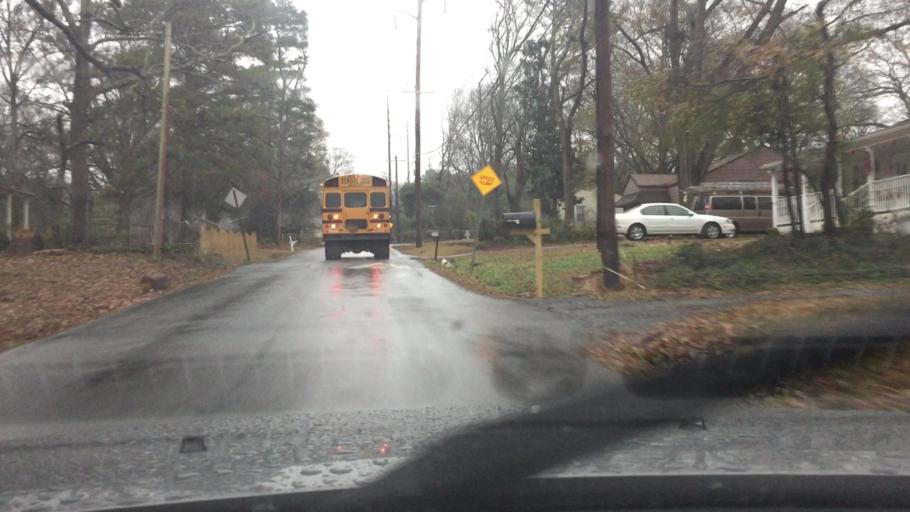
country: US
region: Georgia
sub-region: Cobb County
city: Fair Oaks
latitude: 33.9109
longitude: -84.5400
